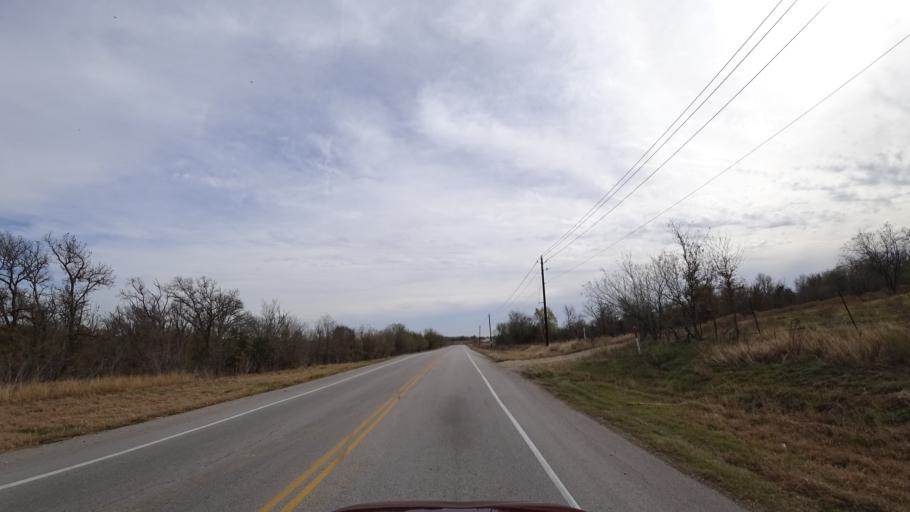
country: US
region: Texas
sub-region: Travis County
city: Garfield
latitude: 30.1617
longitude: -97.6068
